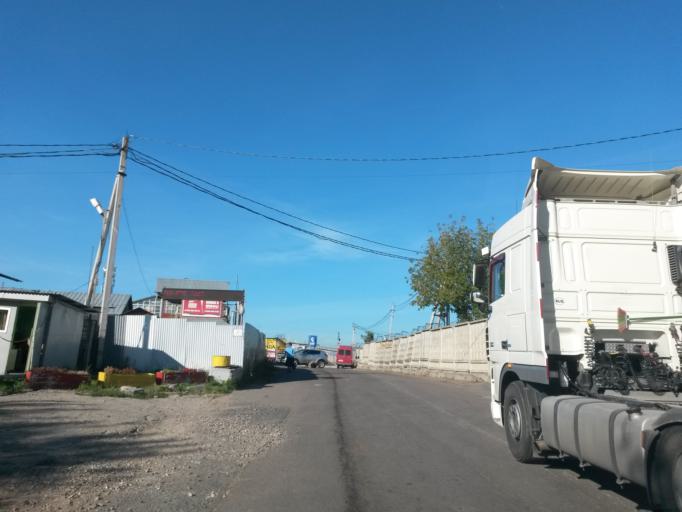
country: RU
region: Moscow
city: Zyablikovo
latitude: 55.6099
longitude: 37.7840
